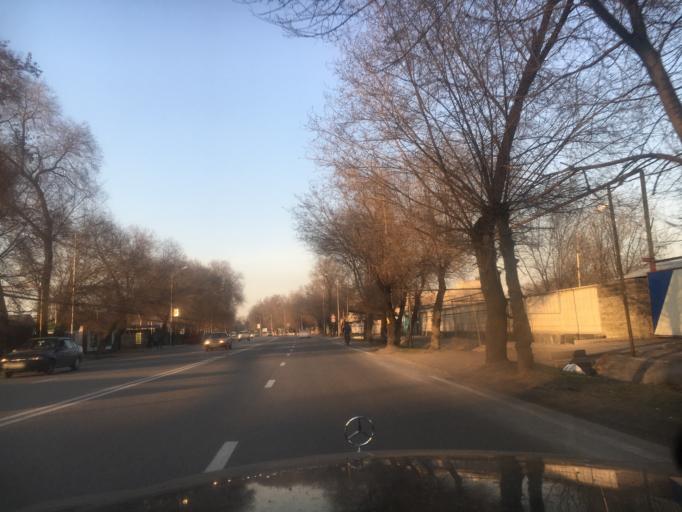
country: KZ
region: Almaty Oblysy
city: Pervomayskiy
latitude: 43.3594
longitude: 76.9803
